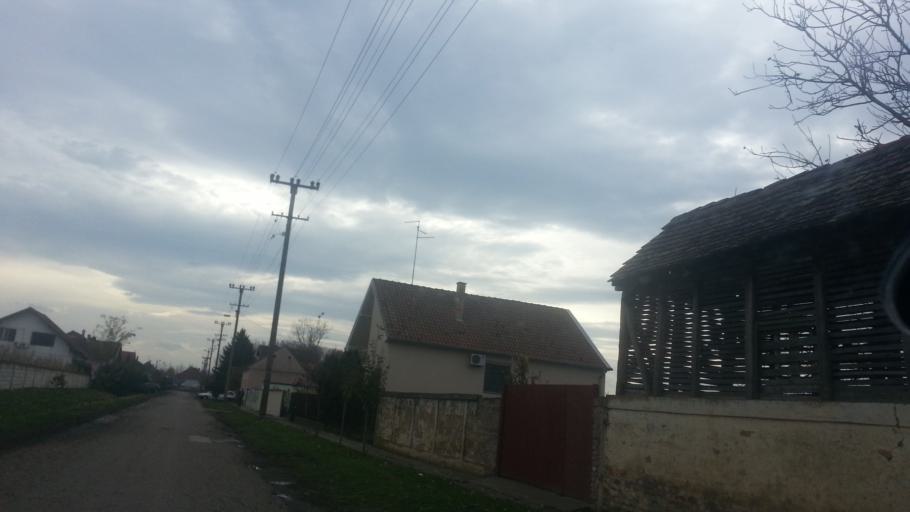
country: RS
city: Golubinci
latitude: 44.9845
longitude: 20.0576
